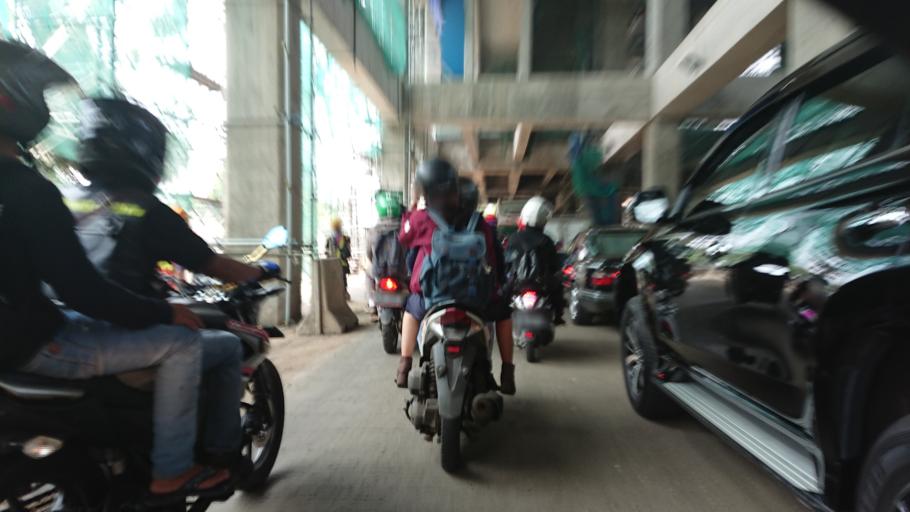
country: ID
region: West Java
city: Pamulang
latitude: -6.2925
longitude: 106.7923
